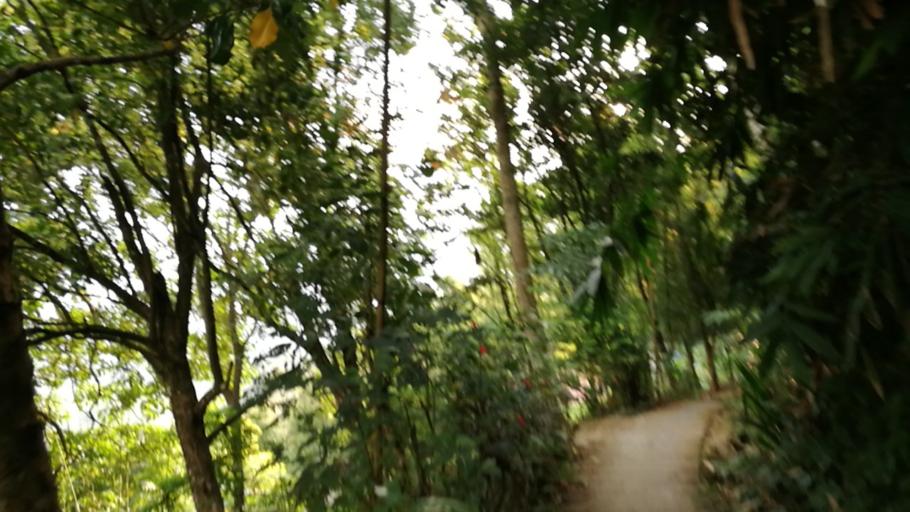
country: ID
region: Bali
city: Munduk
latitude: -8.2672
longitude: 115.0522
